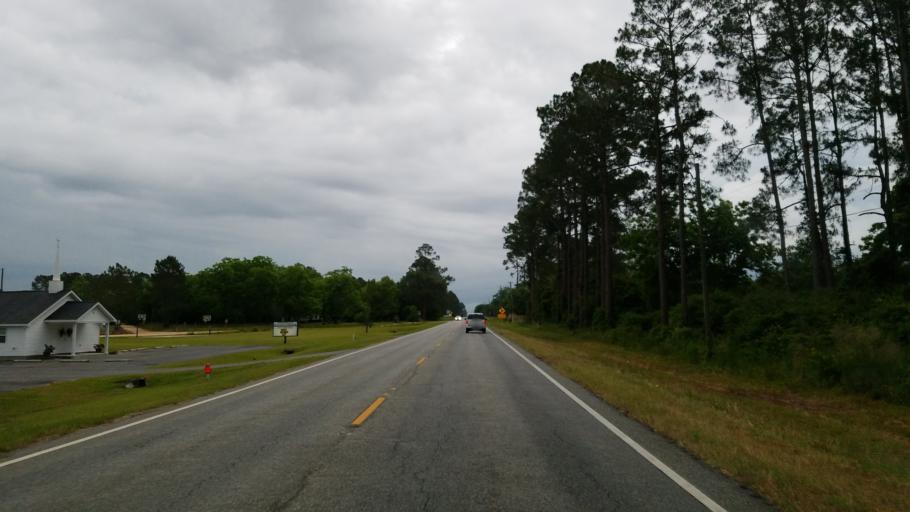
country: US
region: Georgia
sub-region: Berrien County
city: Ray City
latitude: 31.0681
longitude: -83.1733
